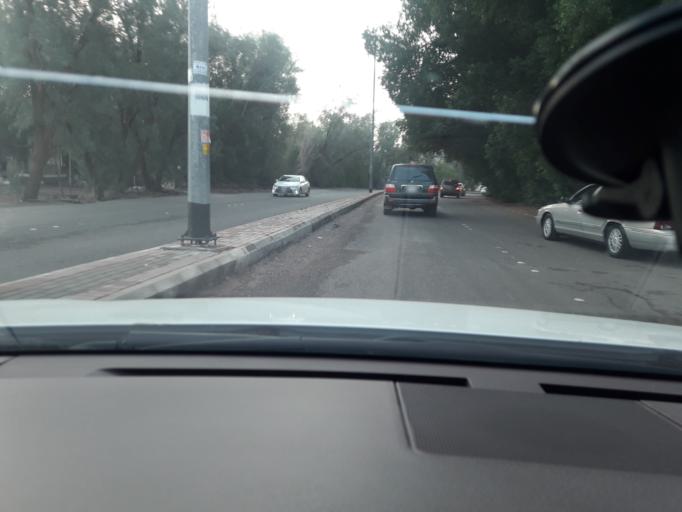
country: SA
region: Al Madinah al Munawwarah
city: Sultanah
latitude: 24.4749
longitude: 39.5694
